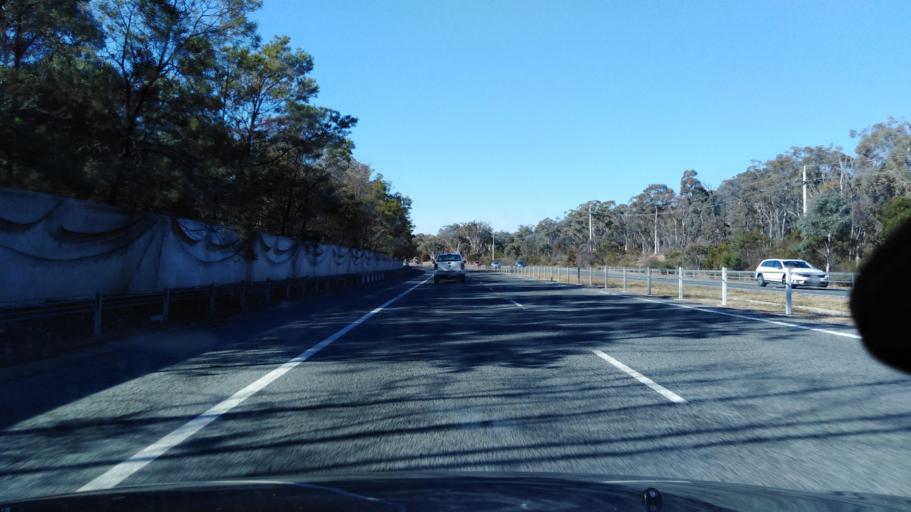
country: AU
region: Australian Capital Territory
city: Acton
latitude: -35.2520
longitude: 149.1021
